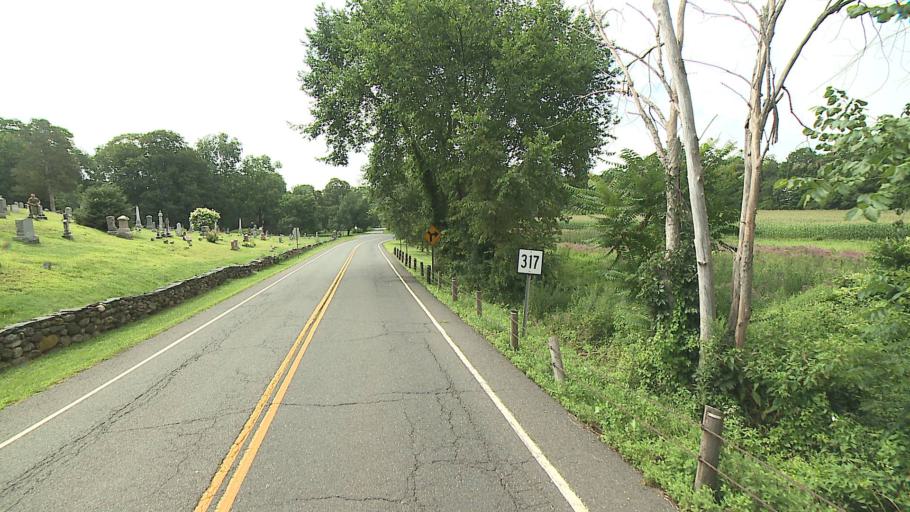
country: US
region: Connecticut
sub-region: Litchfield County
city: Woodbury
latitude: 41.5405
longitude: -73.2093
